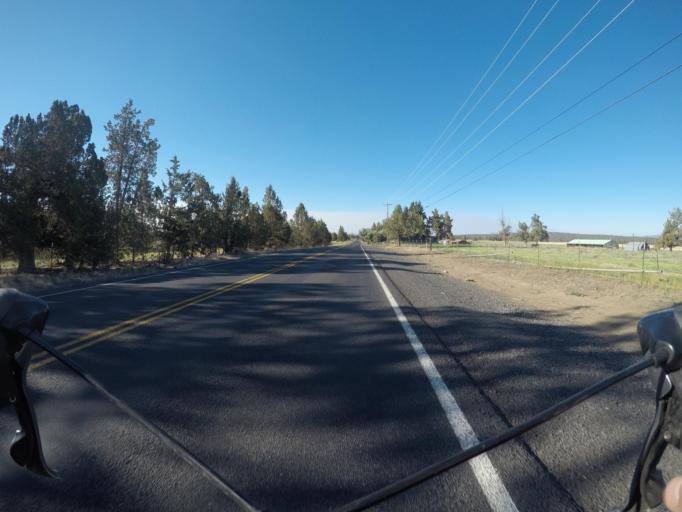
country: US
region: Oregon
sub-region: Deschutes County
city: Redmond
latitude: 44.2055
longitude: -121.2436
